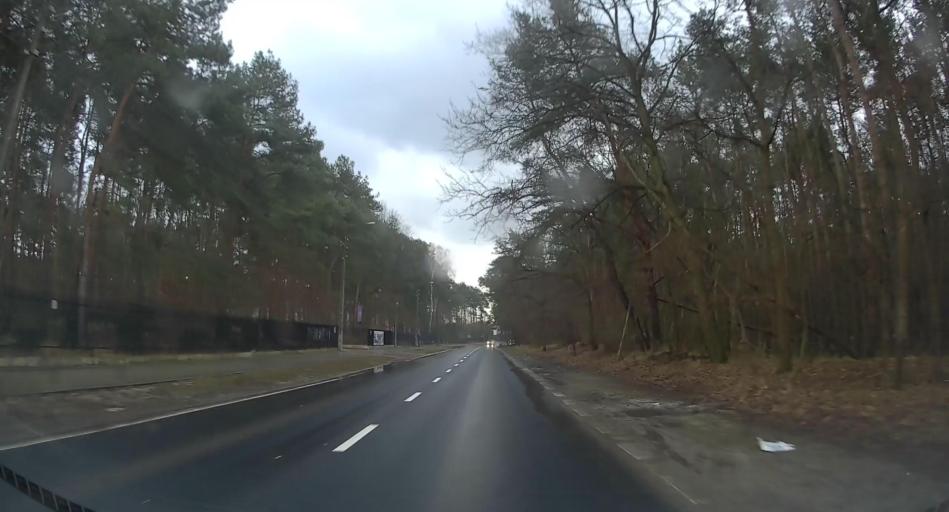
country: PL
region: Masovian Voivodeship
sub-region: Warszawa
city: Wawer
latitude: 52.1781
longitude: 21.1512
